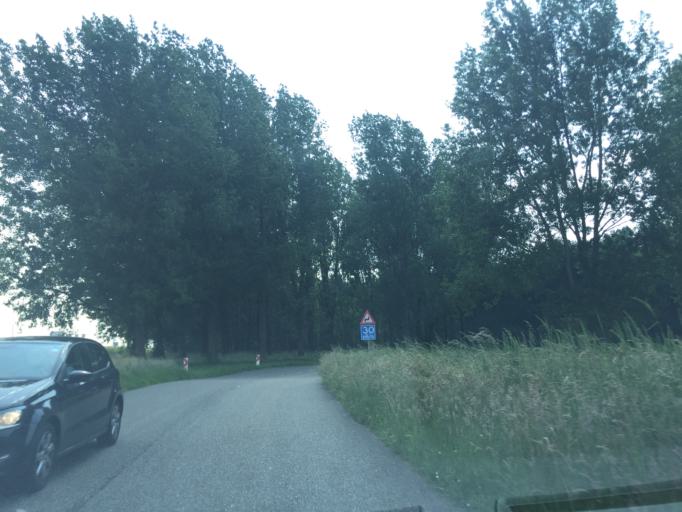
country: NL
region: South Holland
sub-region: Gemeente Voorschoten
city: Voorschoten
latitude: 52.1217
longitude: 4.4755
